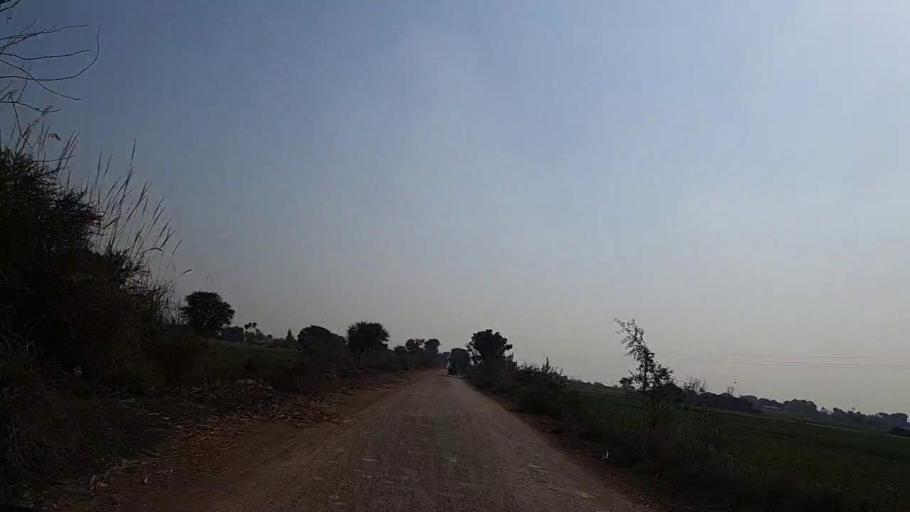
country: PK
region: Sindh
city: Sakrand
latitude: 26.0779
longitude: 68.2899
